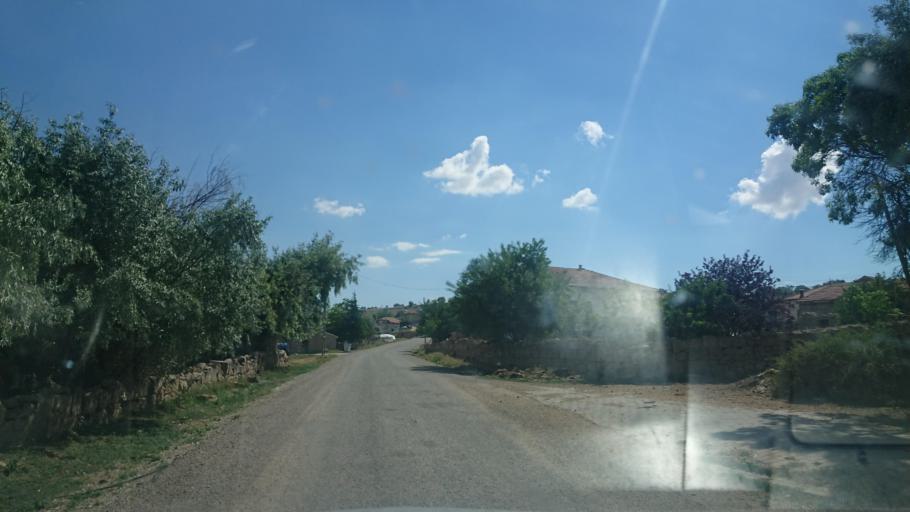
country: TR
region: Aksaray
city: Agacoren
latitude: 38.7742
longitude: 33.7869
